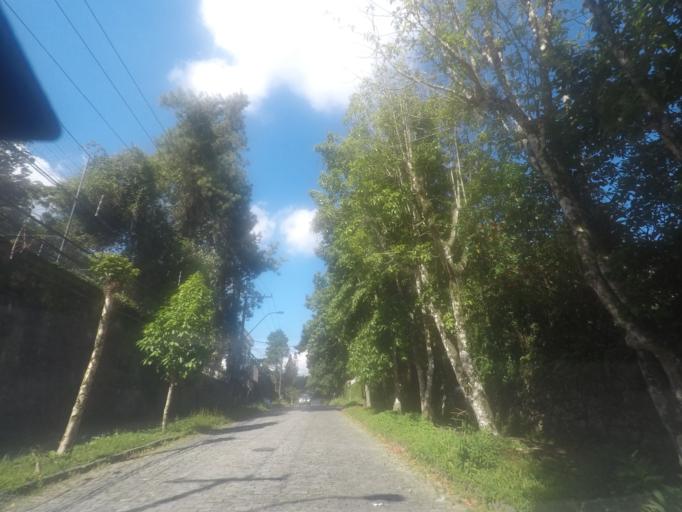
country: BR
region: Rio de Janeiro
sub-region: Petropolis
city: Petropolis
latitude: -22.5226
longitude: -43.2076
